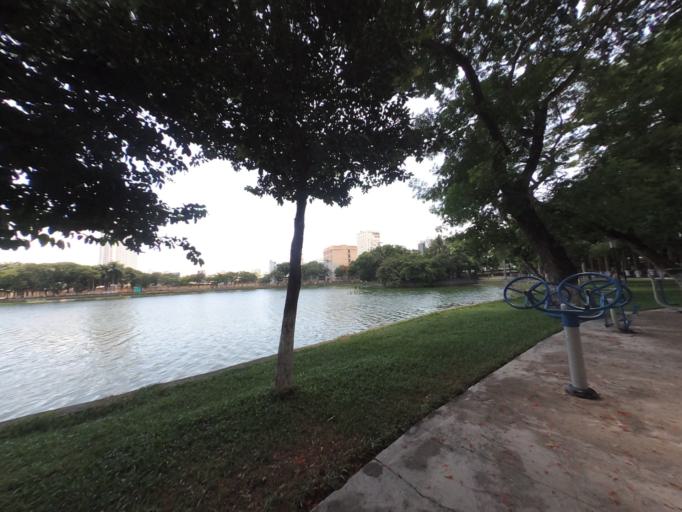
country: VN
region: Da Nang
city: Da Nang
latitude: 16.0604
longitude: 108.2057
